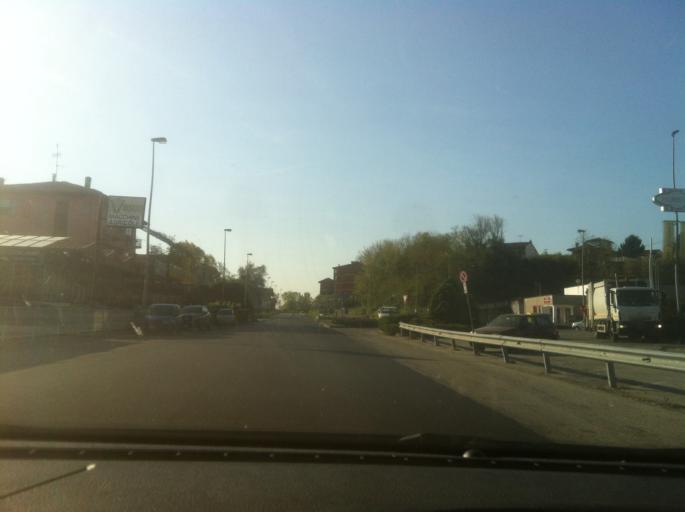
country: IT
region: Piedmont
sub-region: Provincia di Torino
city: Mercenasco
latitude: 45.3614
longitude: 7.8801
